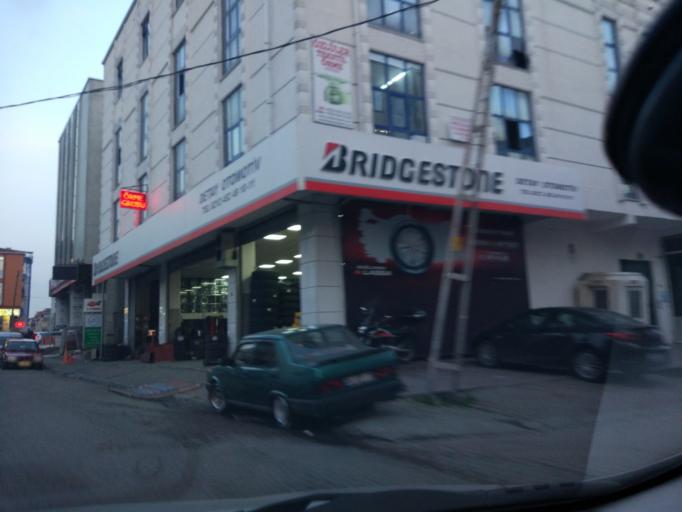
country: TR
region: Istanbul
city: Bahcelievler
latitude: 41.0106
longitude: 28.8283
